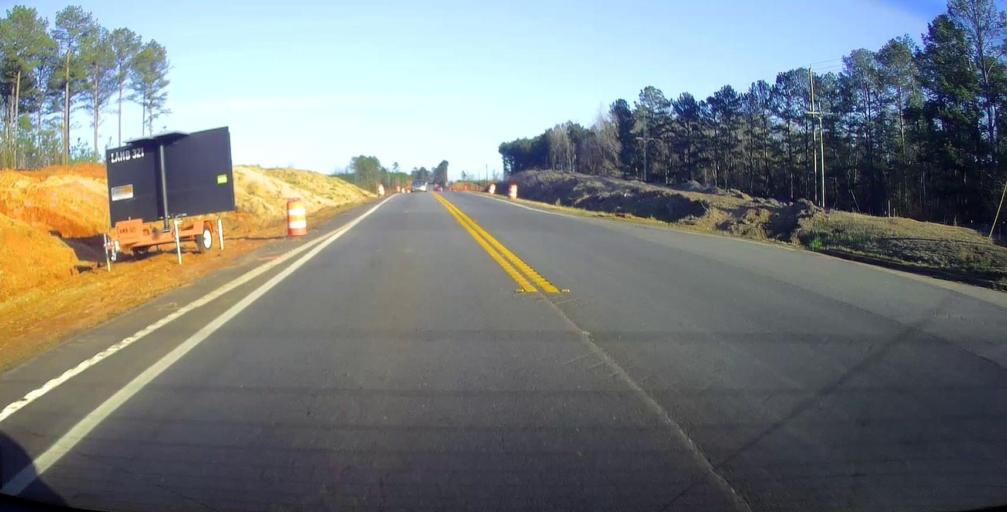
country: US
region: Georgia
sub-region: Troup County
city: West Point
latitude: 32.8766
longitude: -85.1483
